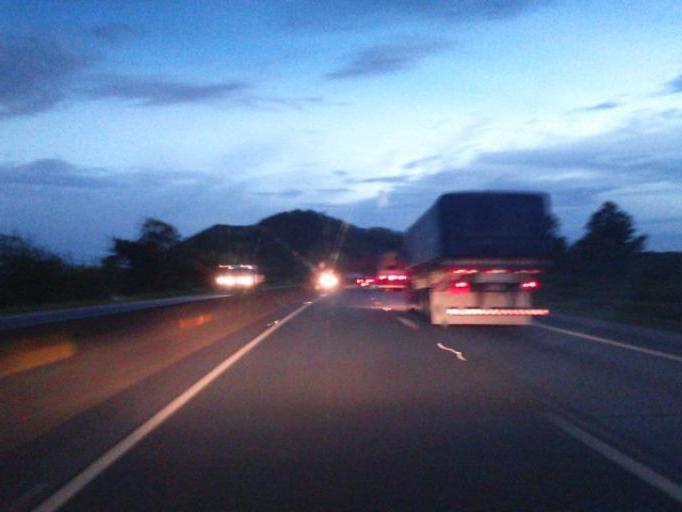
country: BR
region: Santa Catarina
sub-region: Barra Velha
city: Barra Velha
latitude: -26.5643
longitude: -48.7197
